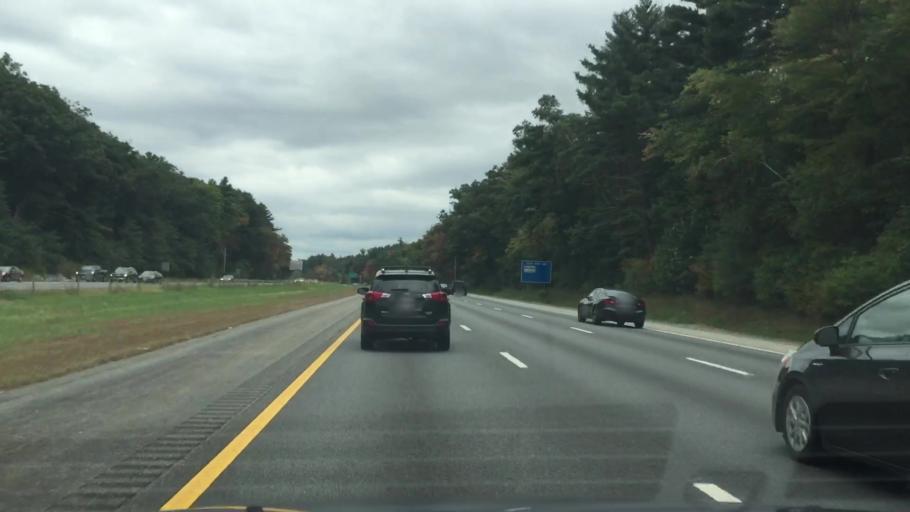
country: US
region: Massachusetts
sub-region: Middlesex County
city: Billerica
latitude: 42.5692
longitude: -71.3031
